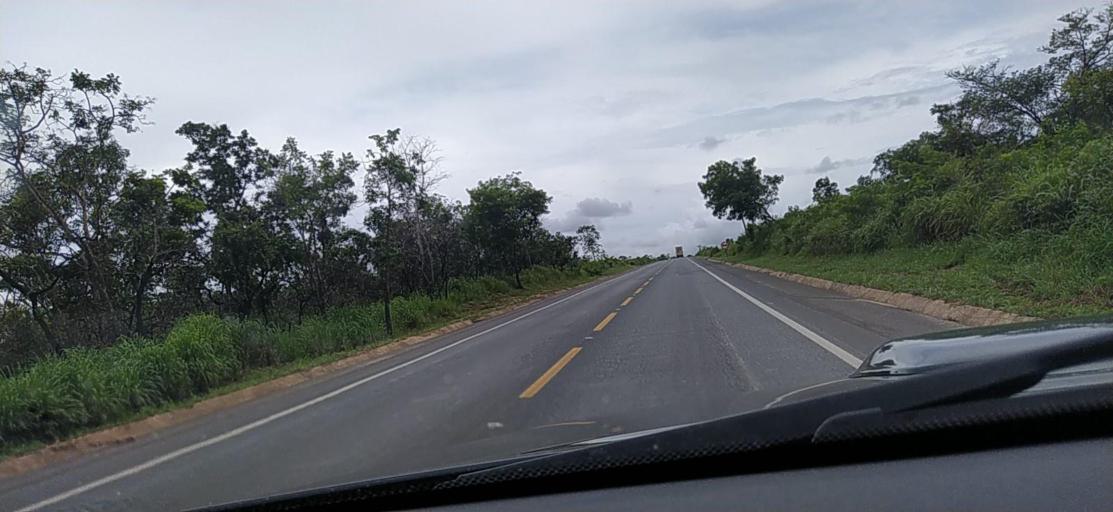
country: BR
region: Minas Gerais
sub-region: Corinto
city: Corinto
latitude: -18.3018
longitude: -44.4120
